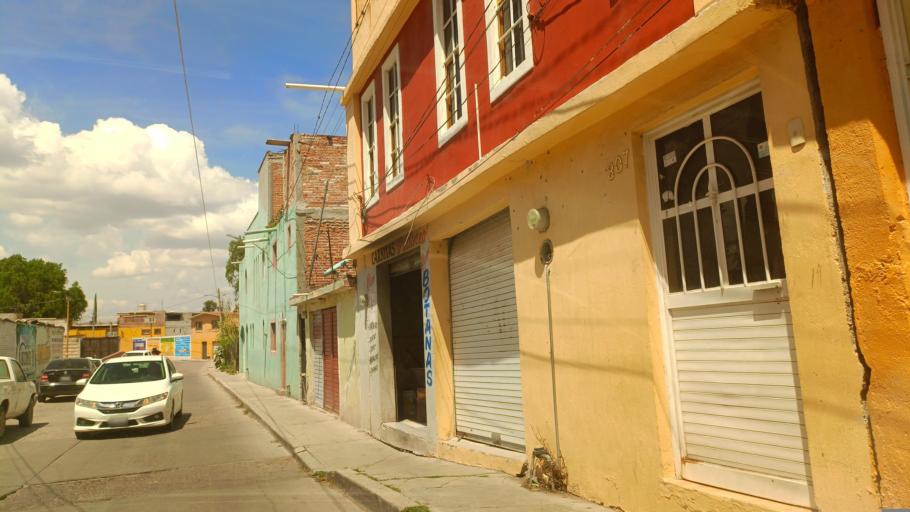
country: MX
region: Guanajuato
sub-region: San Luis de la Paz
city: San Luis de la Paz
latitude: 21.3042
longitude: -100.5166
